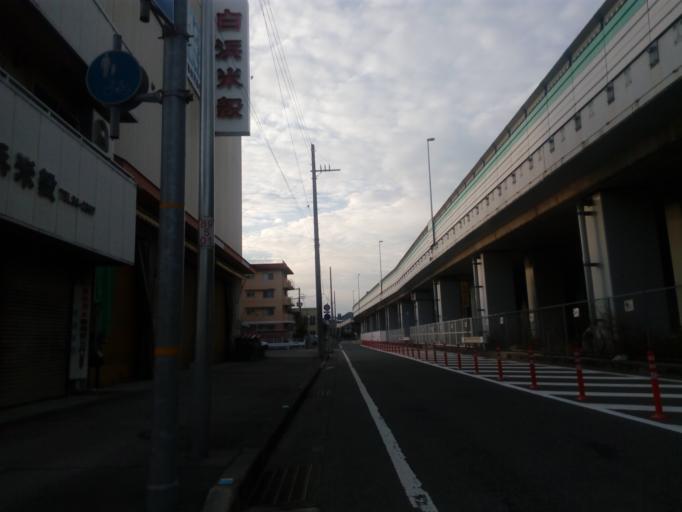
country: JP
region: Hyogo
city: Himeji
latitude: 34.8123
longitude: 134.6803
